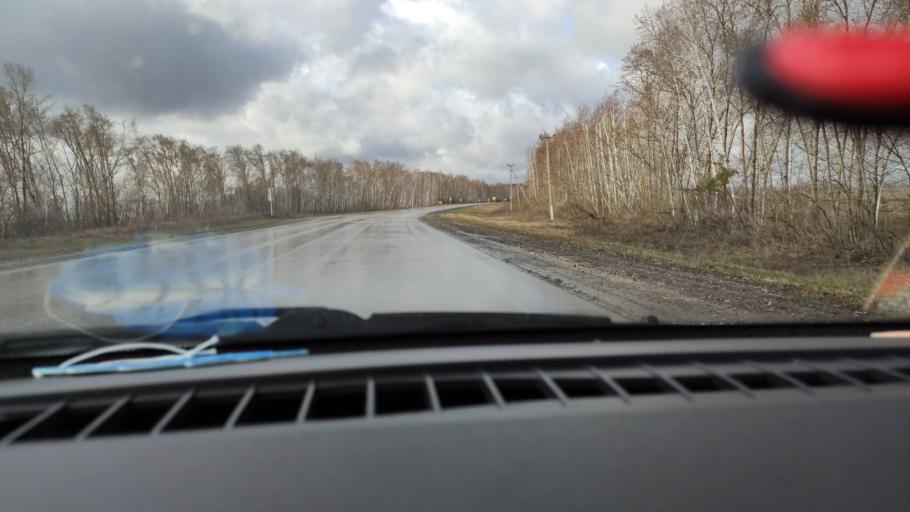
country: RU
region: Samara
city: Yelkhovka
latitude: 54.0624
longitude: 50.3223
